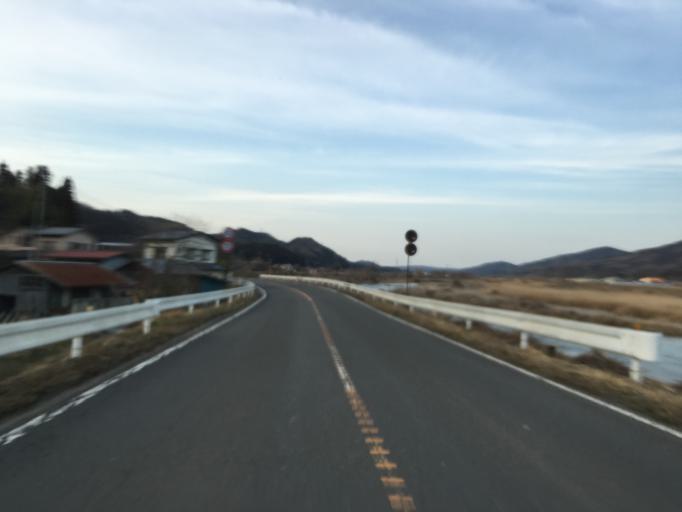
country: JP
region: Ibaraki
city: Daigo
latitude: 36.8949
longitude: 140.4109
